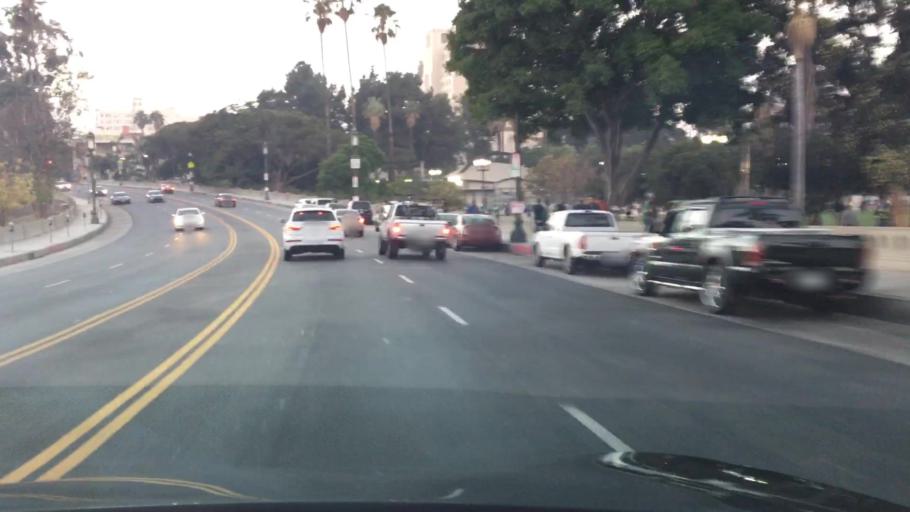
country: US
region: California
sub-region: Los Angeles County
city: Echo Park
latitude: 34.0588
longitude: -118.2768
